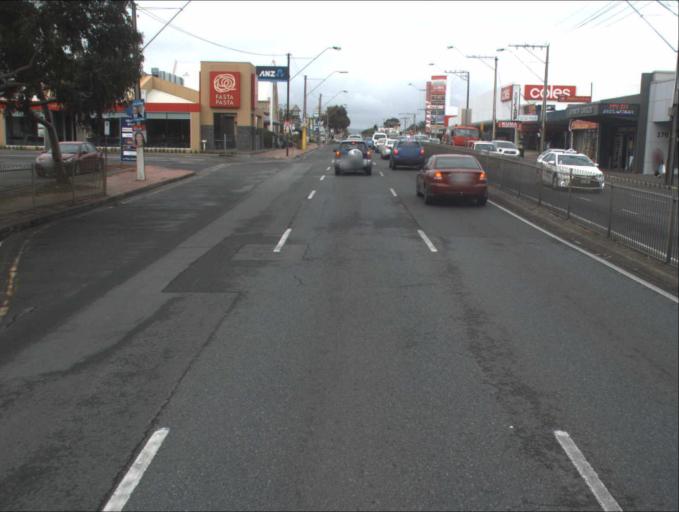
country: AU
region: South Australia
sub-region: Prospect
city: Prospect
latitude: -34.8742
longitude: 138.6021
